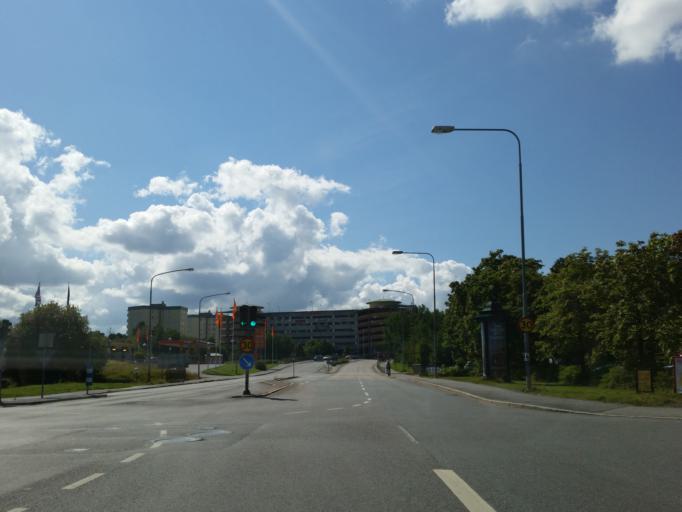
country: SE
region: Stockholm
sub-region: Solna Kommun
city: Solna
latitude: 59.3511
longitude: 18.0046
